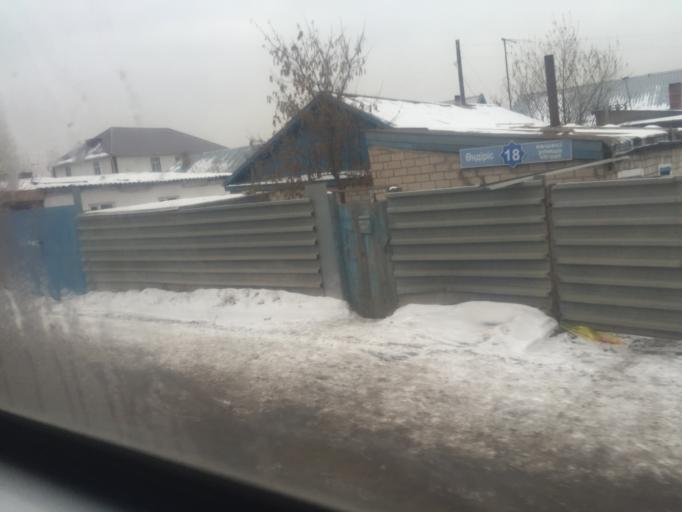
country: KZ
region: Astana Qalasy
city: Astana
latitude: 51.2078
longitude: 71.4078
